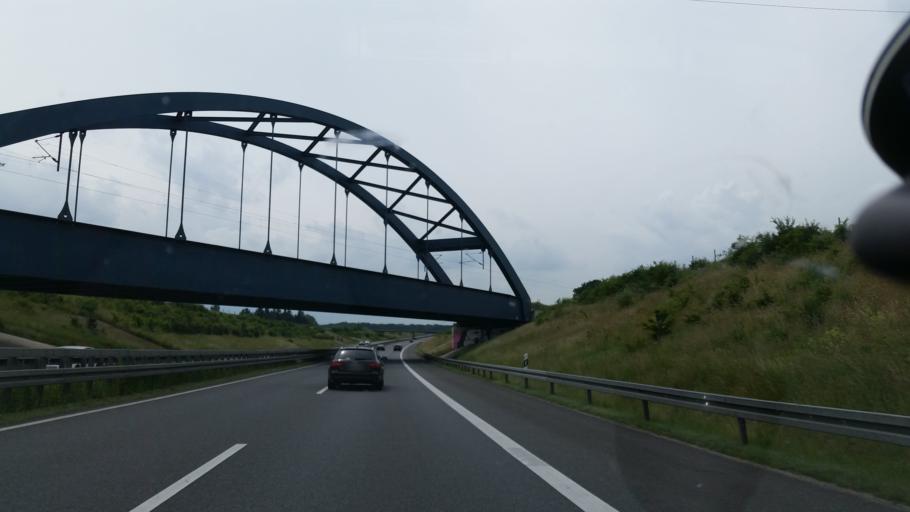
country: DE
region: Lower Saxony
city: Cremlingen
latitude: 52.2711
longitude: 10.7011
